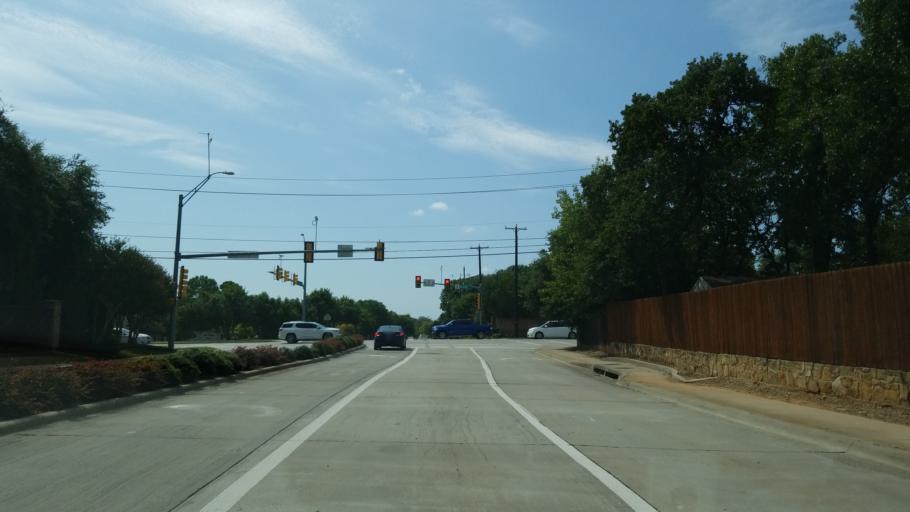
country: US
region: Texas
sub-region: Tarrant County
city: Euless
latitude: 32.8817
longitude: -97.0910
